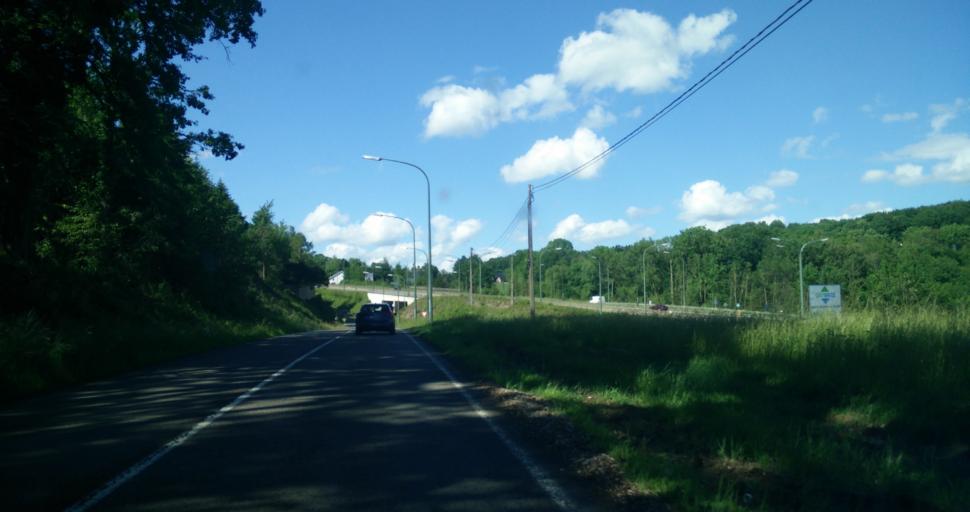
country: BE
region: Wallonia
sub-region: Province du Luxembourg
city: Marche-en-Famenne
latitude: 50.2036
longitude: 5.3673
